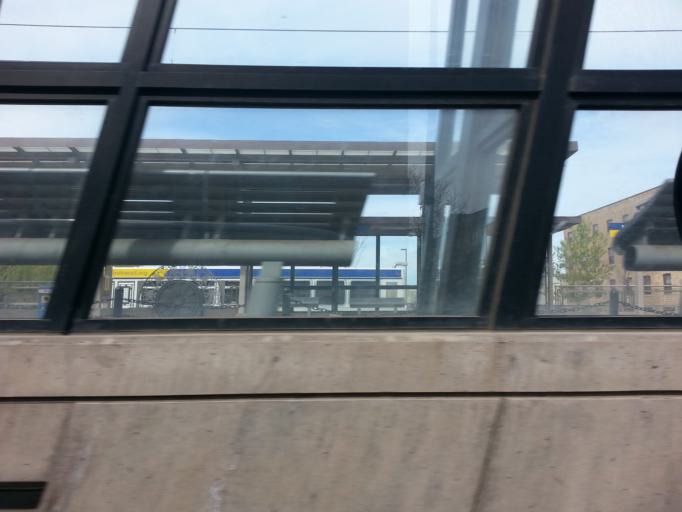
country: US
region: Minnesota
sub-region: Ramsey County
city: Lauderdale
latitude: 44.9630
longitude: -93.1954
